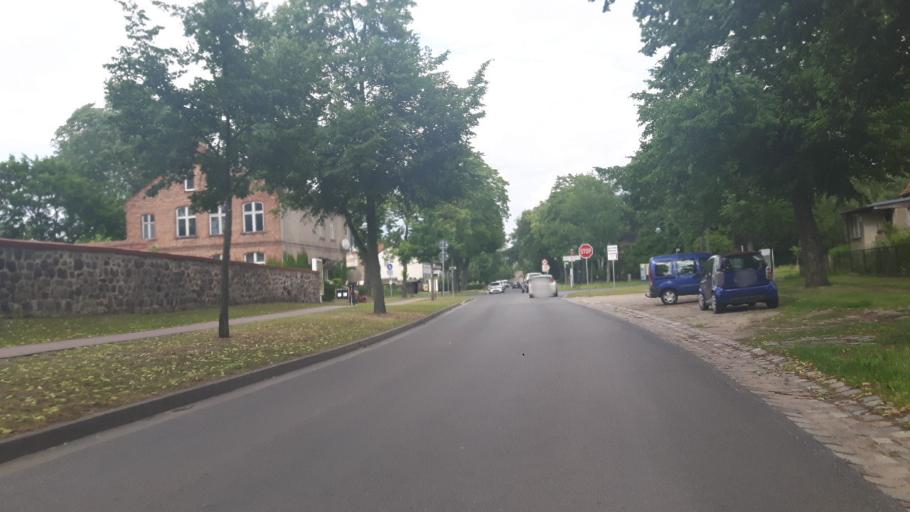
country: DE
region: Brandenburg
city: Bernau bei Berlin
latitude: 52.6625
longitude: 13.6374
